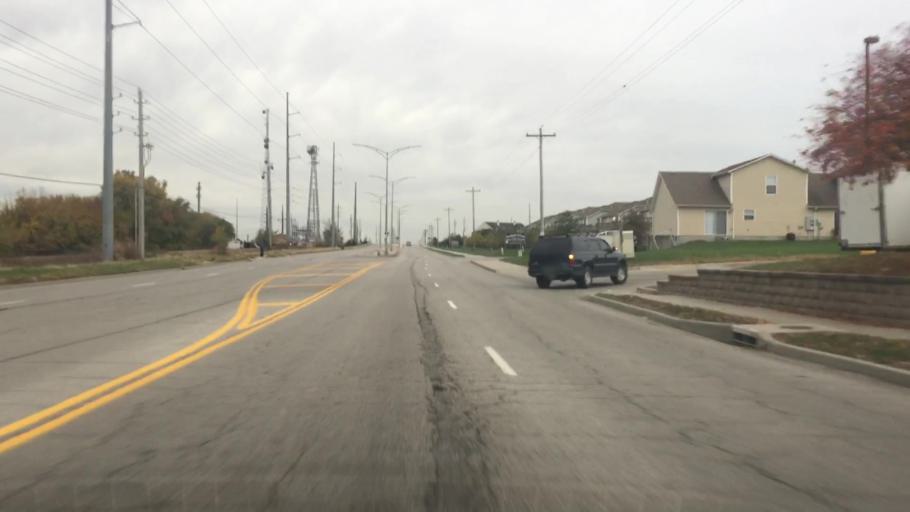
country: US
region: Missouri
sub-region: Cass County
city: Belton
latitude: 38.8119
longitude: -94.5125
